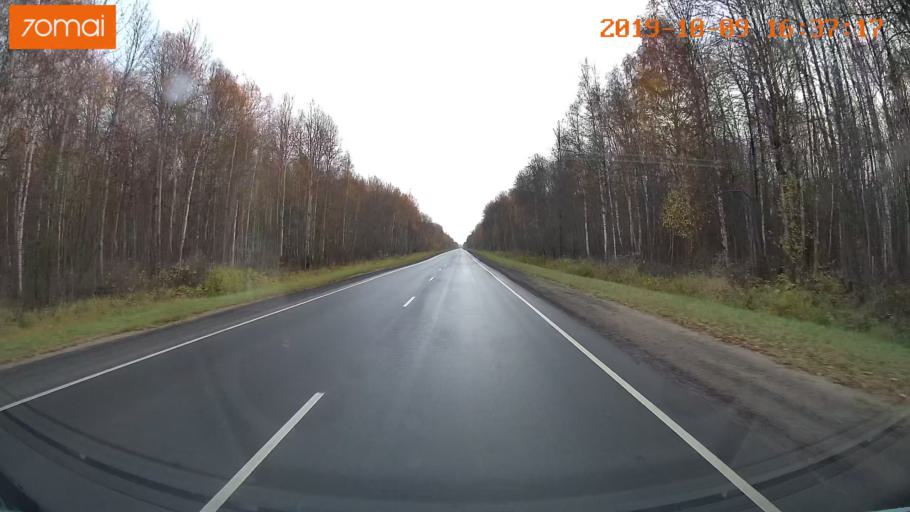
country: RU
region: Kostroma
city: Volgorechensk
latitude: 57.5292
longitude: 41.0228
